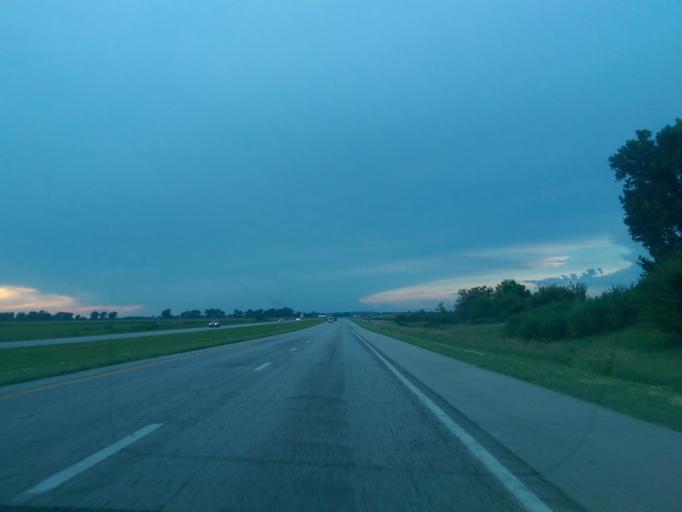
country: US
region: Missouri
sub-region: Holt County
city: Mound City
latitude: 40.1133
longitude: -95.2221
